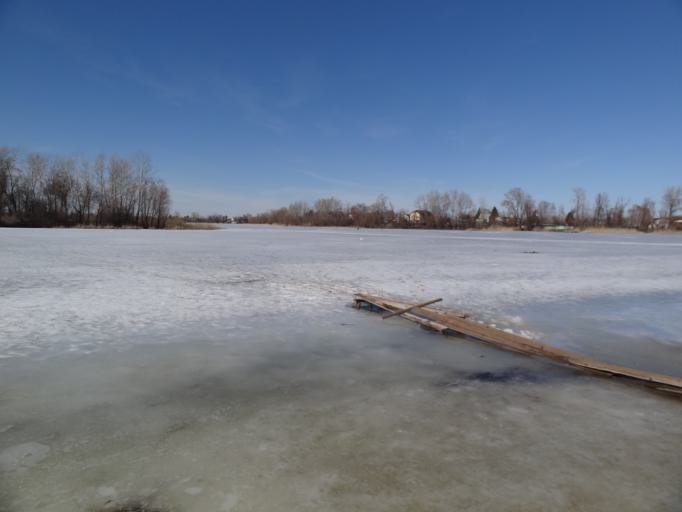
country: RU
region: Saratov
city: Shumeyka
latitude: 51.5170
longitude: 46.2082
